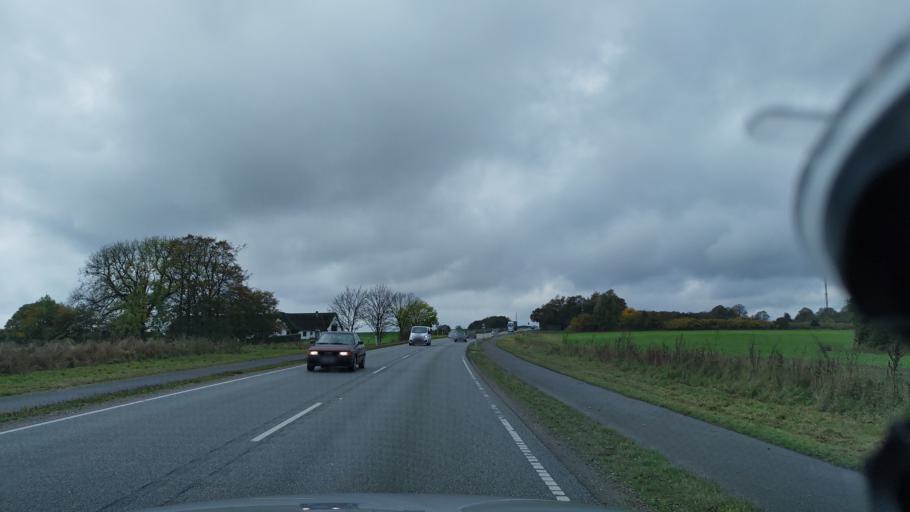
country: DK
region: Zealand
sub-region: Naestved Kommune
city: Fensmark
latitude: 55.2578
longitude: 11.8246
